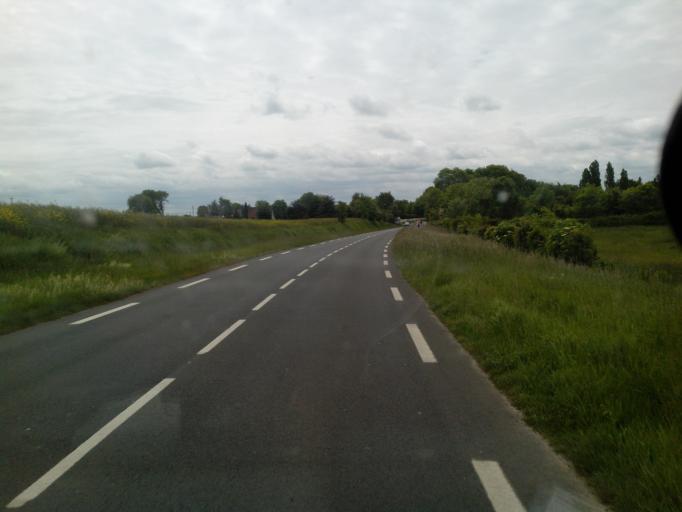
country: FR
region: Lower Normandy
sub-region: Departement du Calvados
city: Amfreville
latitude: 49.2530
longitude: -0.2425
